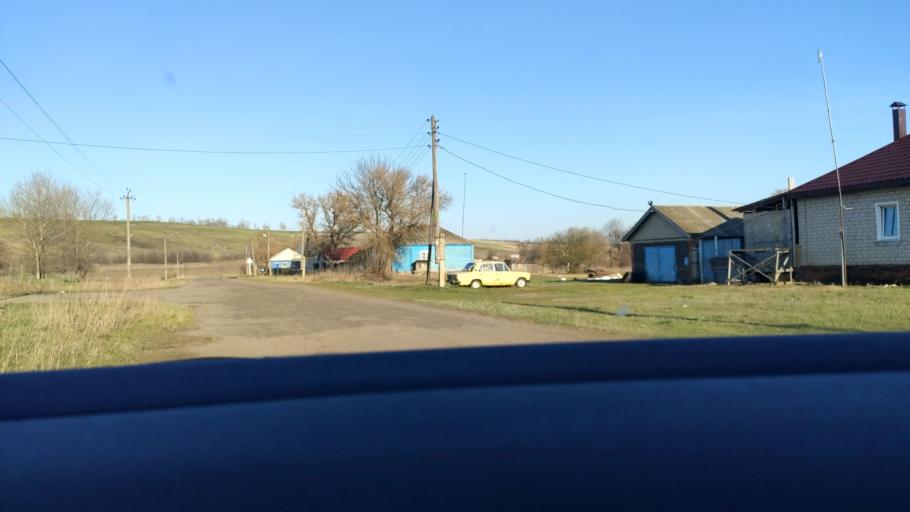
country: RU
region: Voronezj
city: Uryv-Pokrovka
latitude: 51.1478
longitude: 39.0259
